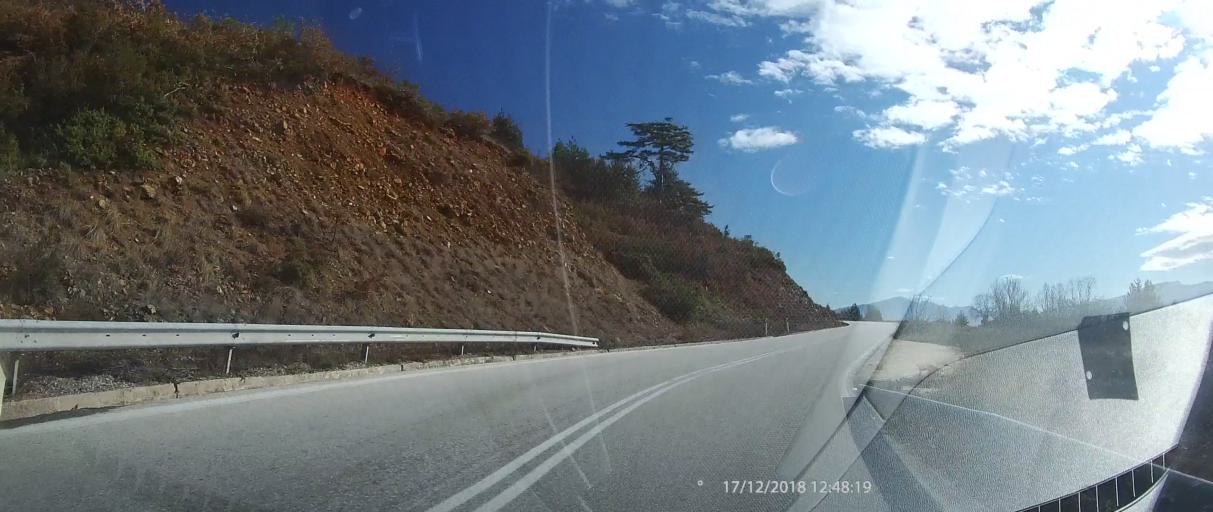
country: GR
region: Thessaly
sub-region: Trikala
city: Kastraki
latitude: 39.7856
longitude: 21.4350
